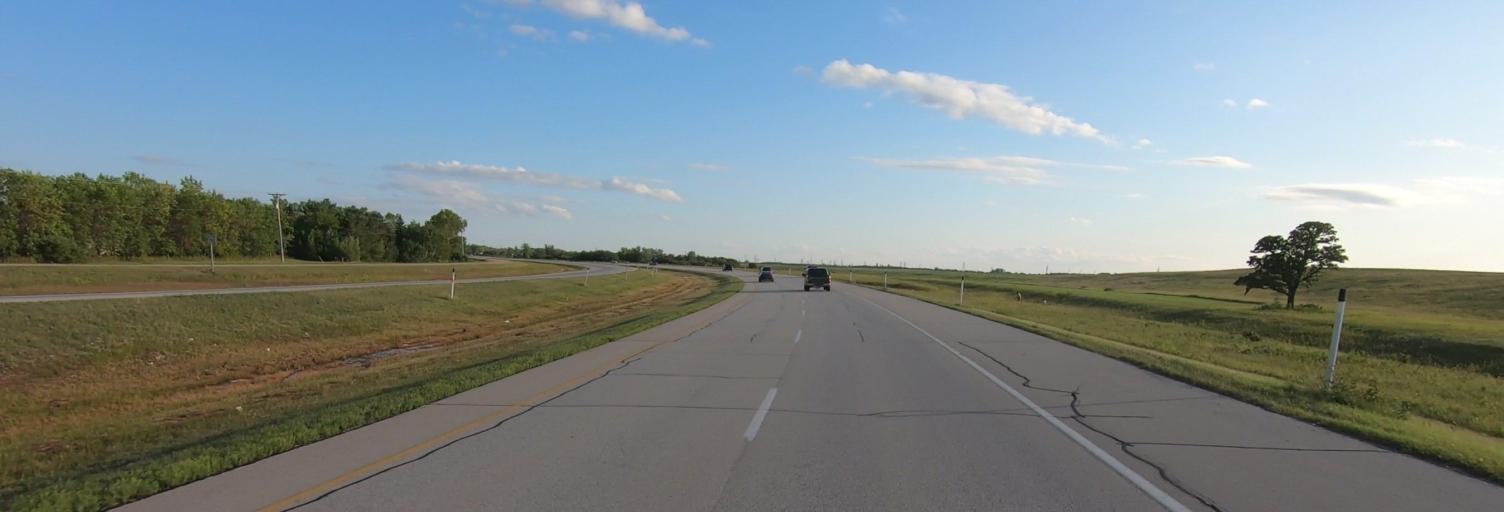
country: CA
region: Manitoba
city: Selkirk
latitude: 49.9921
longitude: -96.9766
